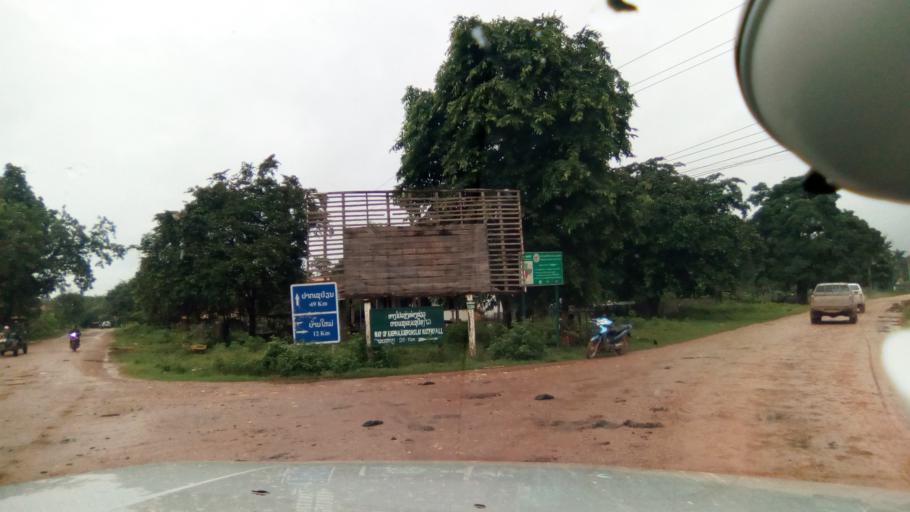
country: LA
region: Attapu
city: Attapu
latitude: 14.6748
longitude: 106.5775
